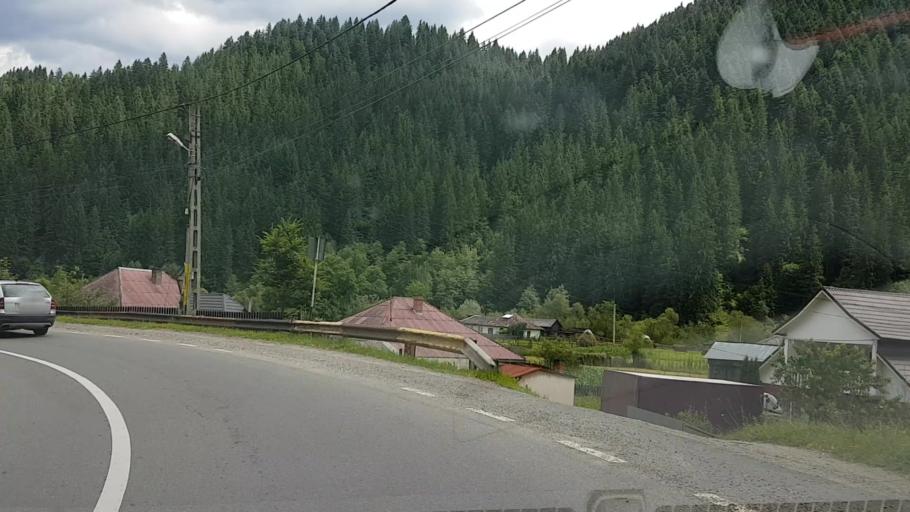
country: RO
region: Neamt
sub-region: Comuna Farcasa
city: Farcasa
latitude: 47.1491
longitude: 25.8481
